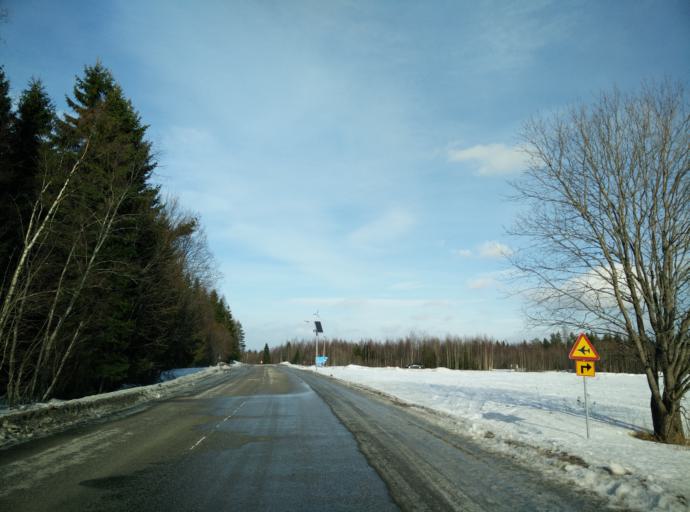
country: SE
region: Vaesternorrland
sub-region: Sundsvalls Kommun
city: Njurundabommen
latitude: 62.2357
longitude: 17.3823
